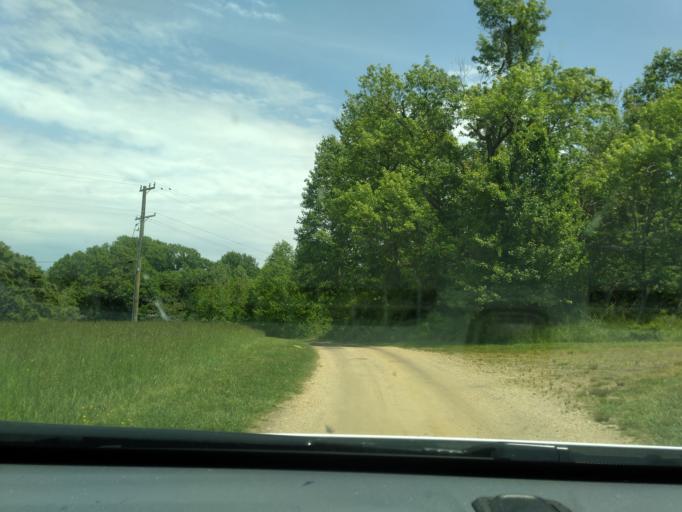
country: US
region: Maryland
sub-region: Prince George's County
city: Marlboro Meadows
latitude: 38.8491
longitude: -76.7060
